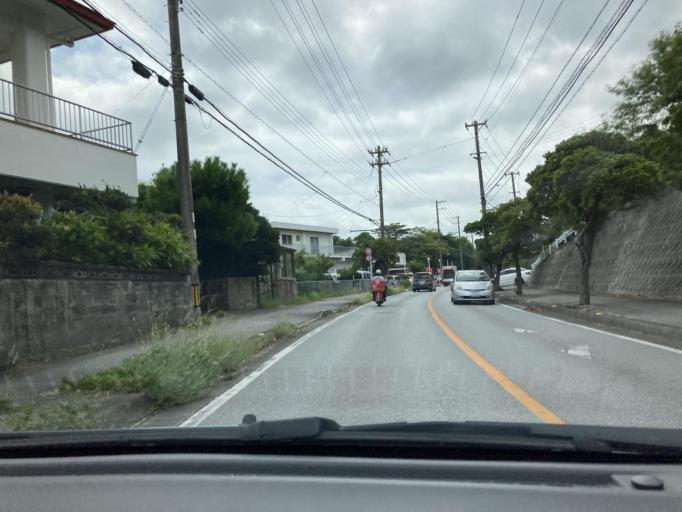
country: JP
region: Okinawa
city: Ginowan
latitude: 26.2818
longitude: 127.7849
